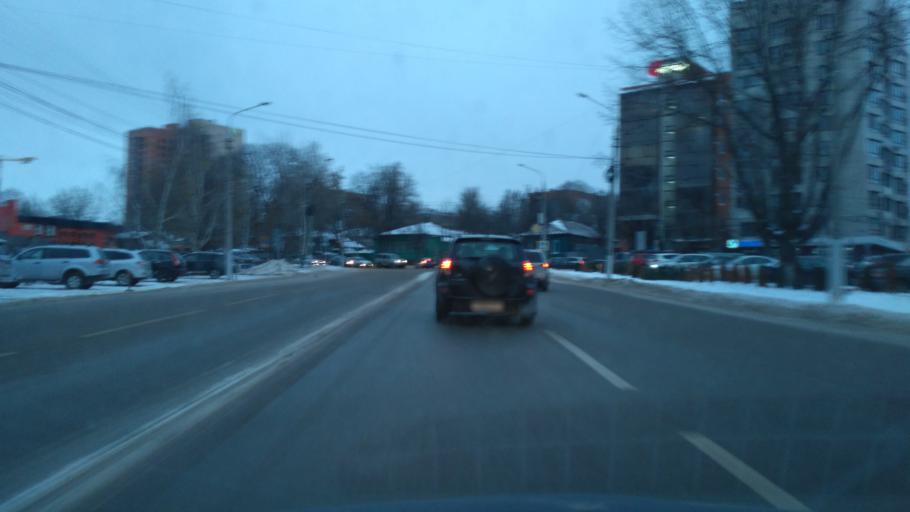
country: RU
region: Tula
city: Tula
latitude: 54.1916
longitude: 37.6022
